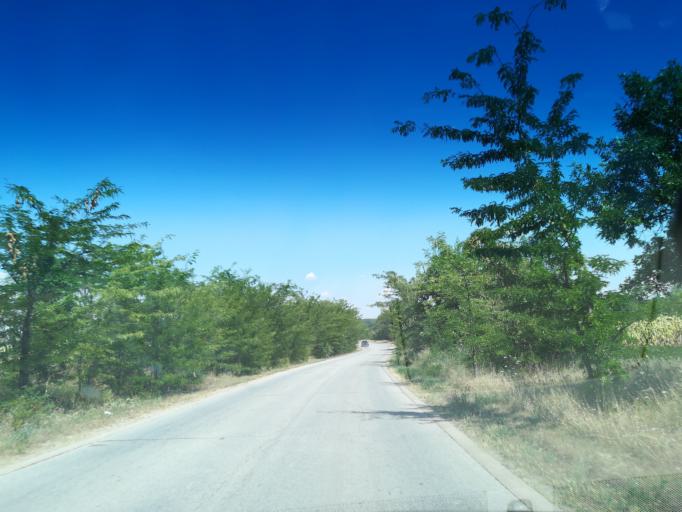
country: BG
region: Plovdiv
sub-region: Obshtina Sadovo
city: Sadovo
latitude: 42.0398
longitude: 25.1315
